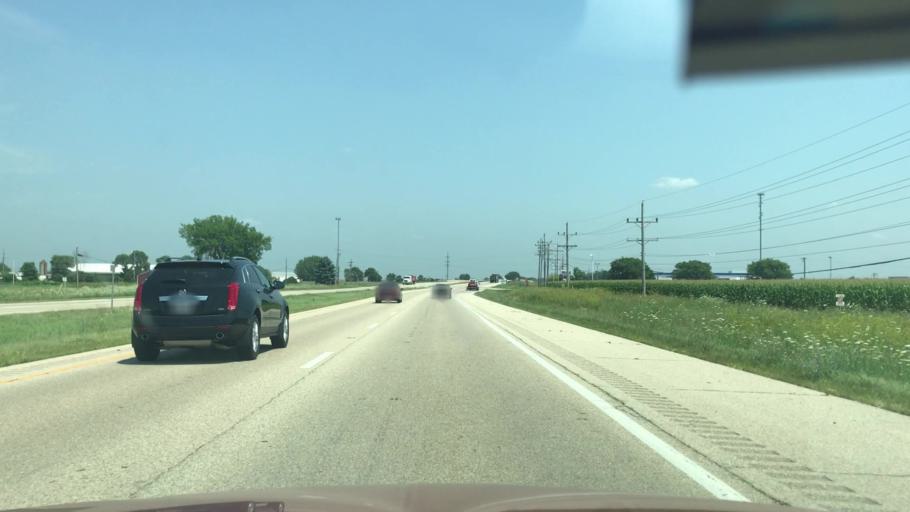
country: US
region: Illinois
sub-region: Winnebago County
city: Cherry Valley
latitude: 42.2391
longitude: -88.9231
